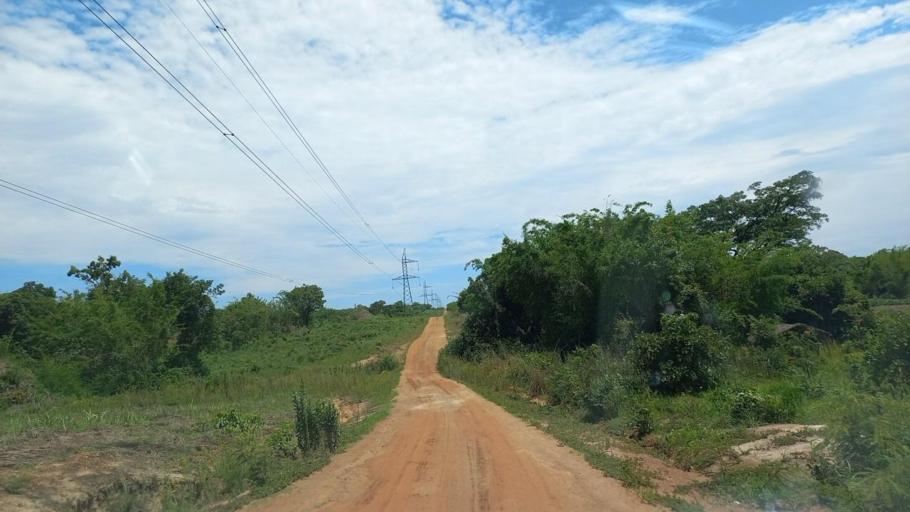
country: ZM
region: Copperbelt
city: Kitwe
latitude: -12.8136
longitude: 28.3579
